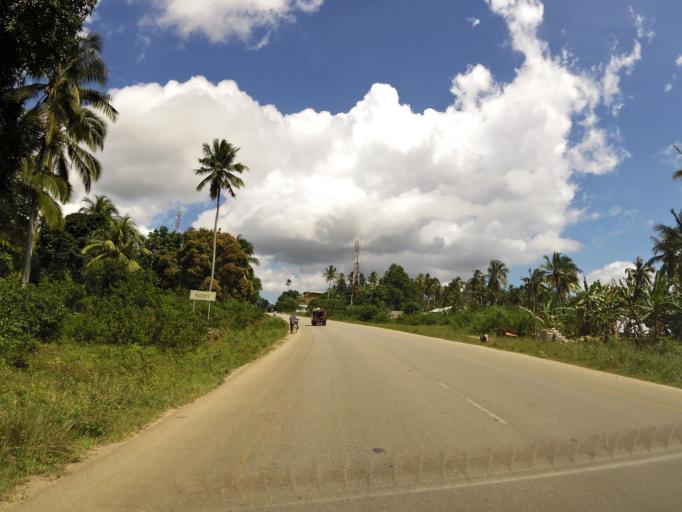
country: TZ
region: Zanzibar Central/South
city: Koani
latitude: -6.1360
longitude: 39.2900
